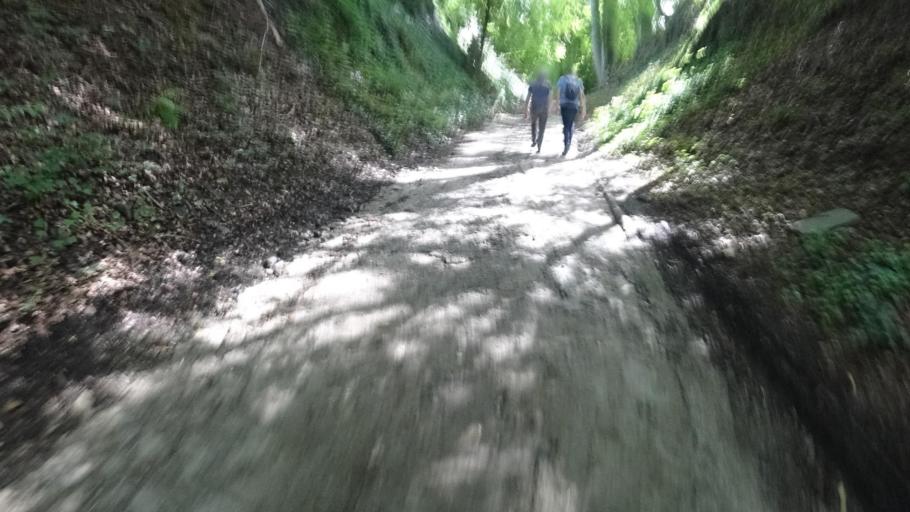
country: BE
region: Wallonia
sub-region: Province du Brabant Wallon
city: Villers-la-Ville
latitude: 50.5896
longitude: 4.5269
